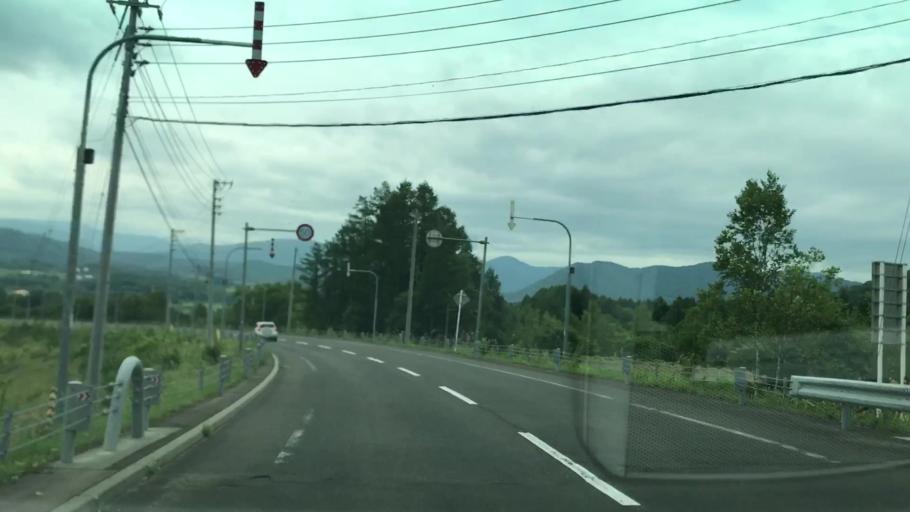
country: JP
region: Hokkaido
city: Yoichi
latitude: 43.1106
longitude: 140.8192
